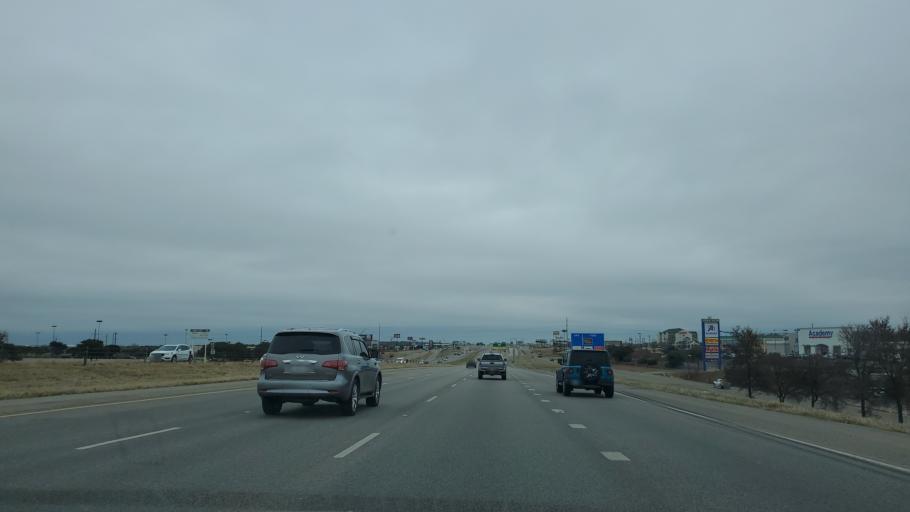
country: US
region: Texas
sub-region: Bell County
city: Killeen
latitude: 31.0906
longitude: -97.7196
